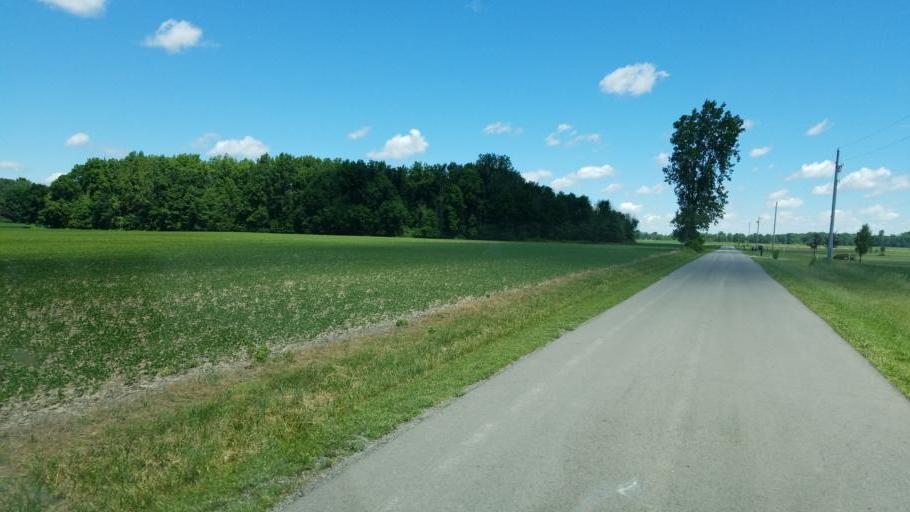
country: US
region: Ohio
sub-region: Morrow County
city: Mount Gilead
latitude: 40.6415
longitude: -82.9374
